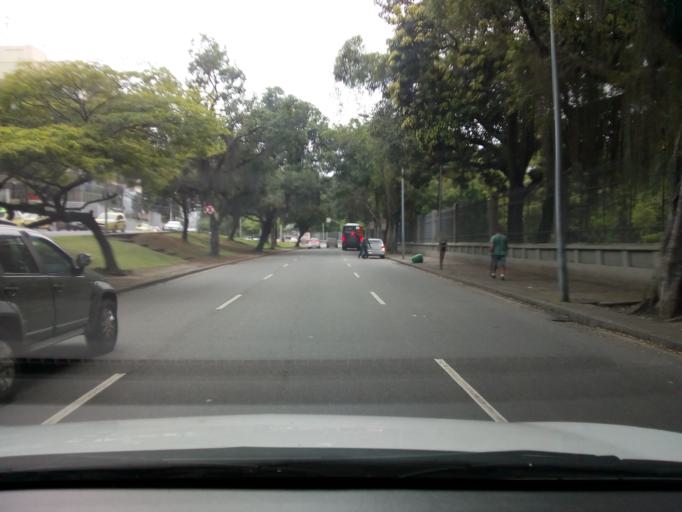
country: BR
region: Rio de Janeiro
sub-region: Rio De Janeiro
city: Rio de Janeiro
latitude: -22.9068
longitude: -43.2213
